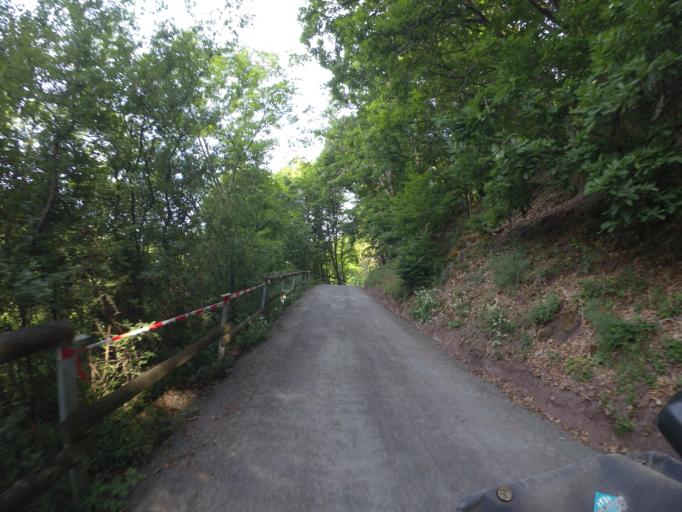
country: DE
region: Saarland
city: Nonnweiler
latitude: 49.6170
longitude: 6.9431
